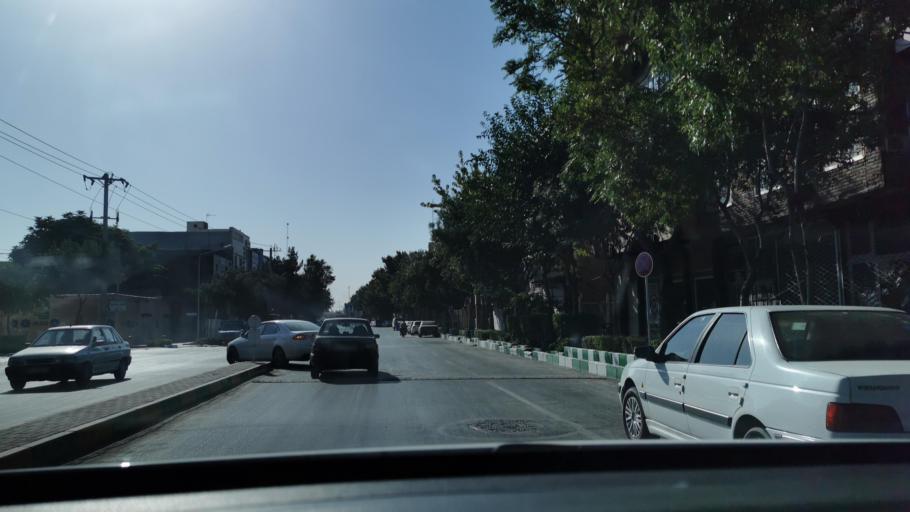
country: IR
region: Razavi Khorasan
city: Mashhad
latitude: 36.2973
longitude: 59.6223
